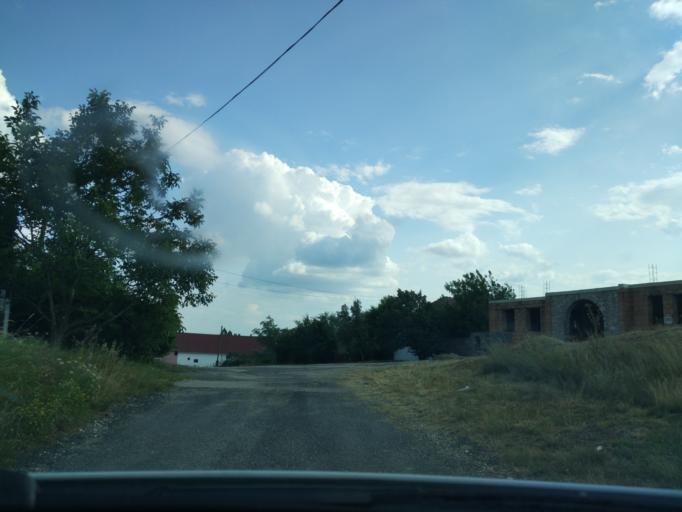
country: HU
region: Veszprem
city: Varpalota
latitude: 47.2040
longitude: 18.1756
